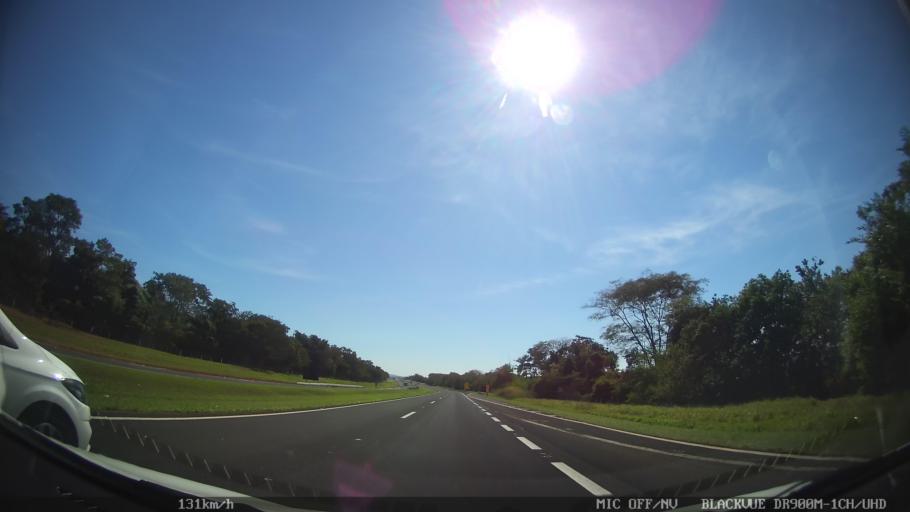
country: BR
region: Sao Paulo
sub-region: Sao Simao
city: Sao Simao
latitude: -21.6159
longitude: -47.6159
